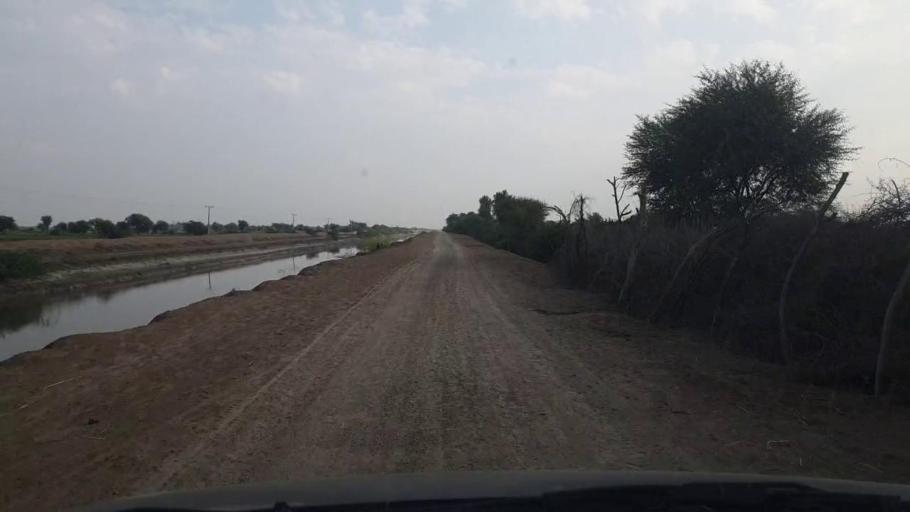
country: PK
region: Sindh
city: Badin
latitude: 24.5216
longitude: 68.6820
